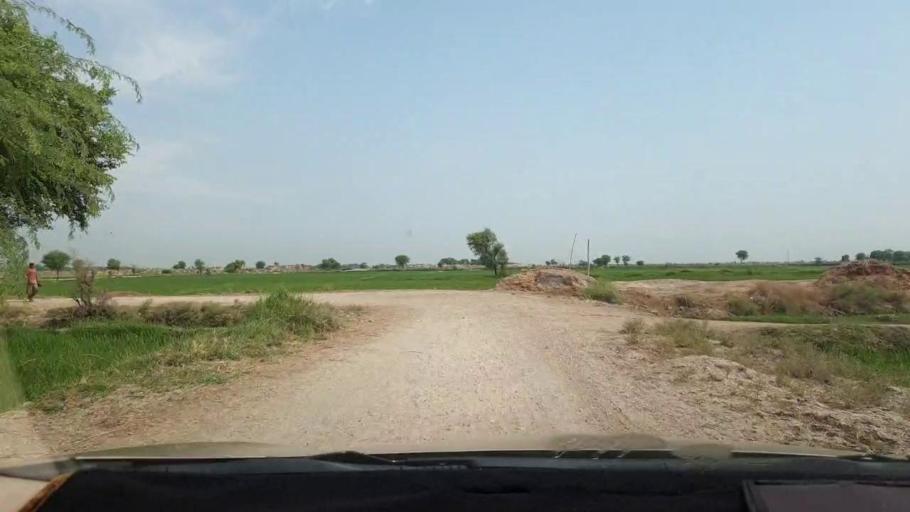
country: PK
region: Sindh
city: Larkana
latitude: 27.6809
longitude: 68.2194
